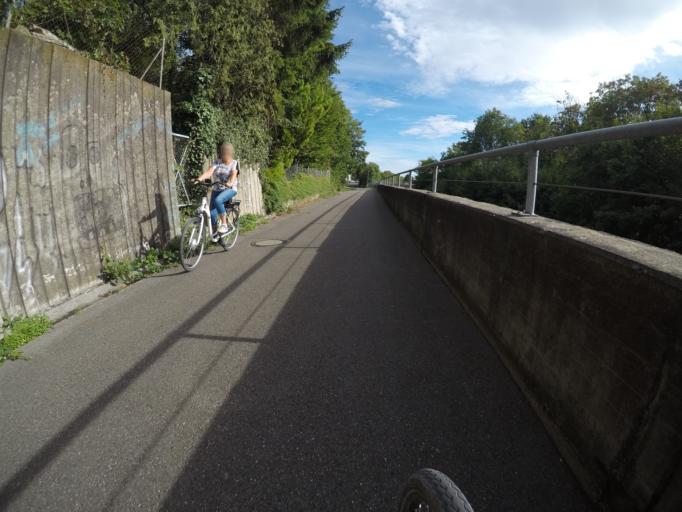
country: DE
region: Baden-Wuerttemberg
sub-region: Regierungsbezirk Stuttgart
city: Marbach am Neckar
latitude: 48.9073
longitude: 9.2603
